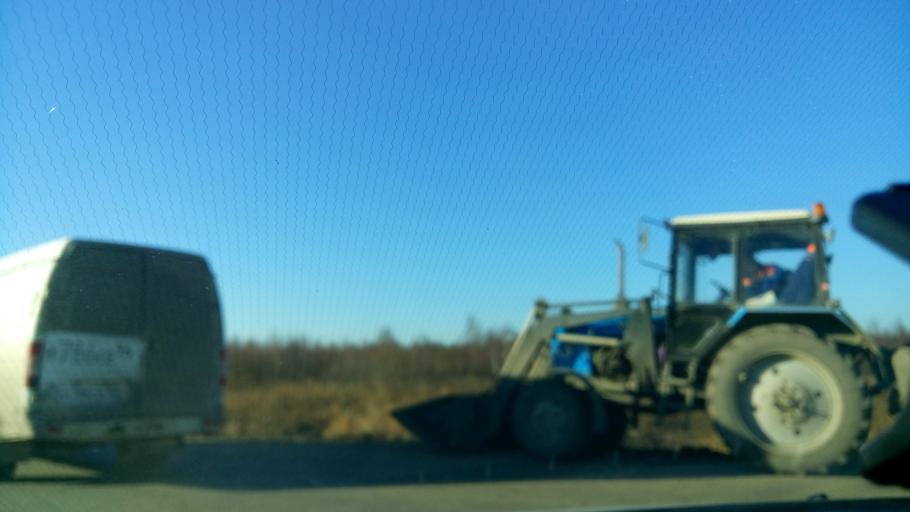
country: RU
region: Sverdlovsk
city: Sovkhoznyy
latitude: 56.7335
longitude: 60.5380
